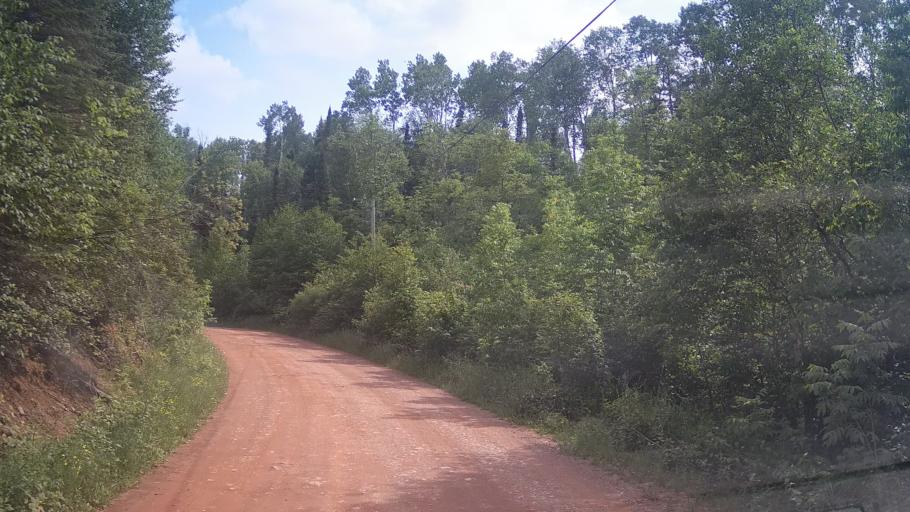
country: CA
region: Ontario
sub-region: Thunder Bay District
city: Thunder Bay
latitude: 48.6667
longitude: -88.6655
